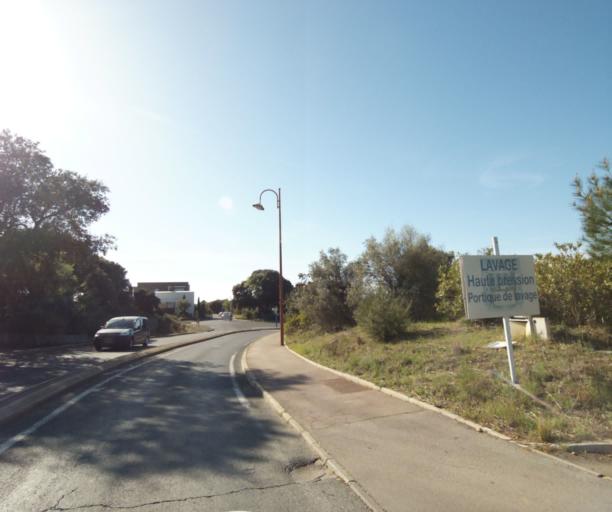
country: FR
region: Languedoc-Roussillon
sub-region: Departement de l'Herault
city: Perols
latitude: 43.5699
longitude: 3.9414
